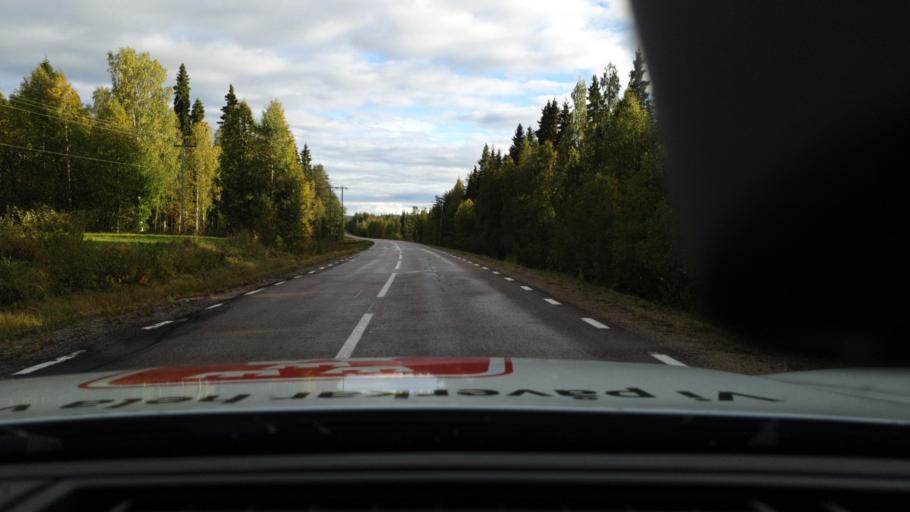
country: SE
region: Norrbotten
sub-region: Overkalix Kommun
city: OEverkalix
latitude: 66.6411
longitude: 22.7225
